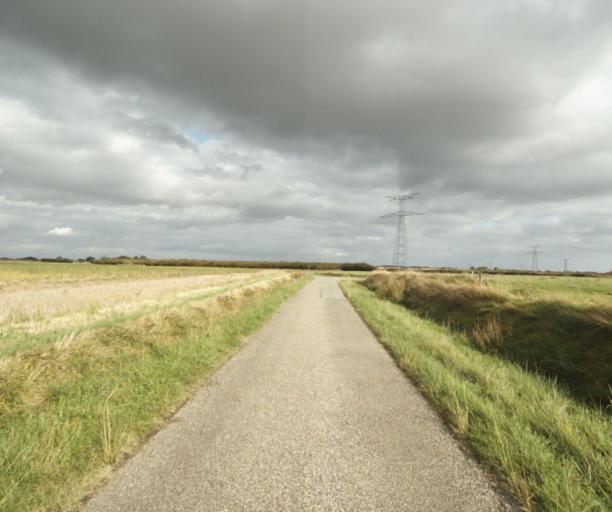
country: FR
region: Midi-Pyrenees
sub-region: Departement du Tarn-et-Garonne
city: Finhan
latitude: 43.9006
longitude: 1.1143
